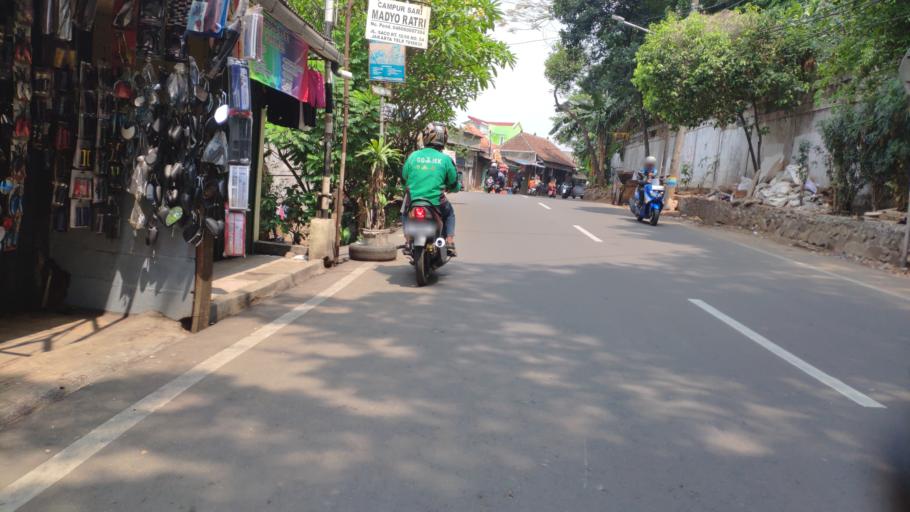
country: ID
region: West Java
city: Pamulang
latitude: -6.3064
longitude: 106.8166
